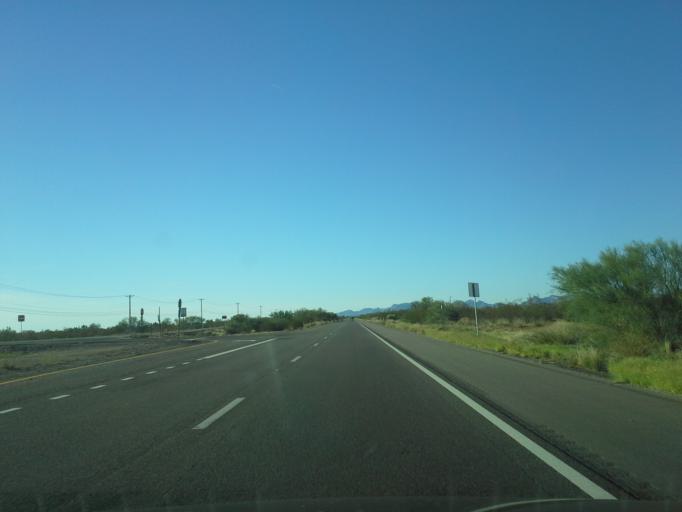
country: US
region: Arizona
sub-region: Pinal County
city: Gold Camp
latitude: 33.3113
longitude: -111.4114
